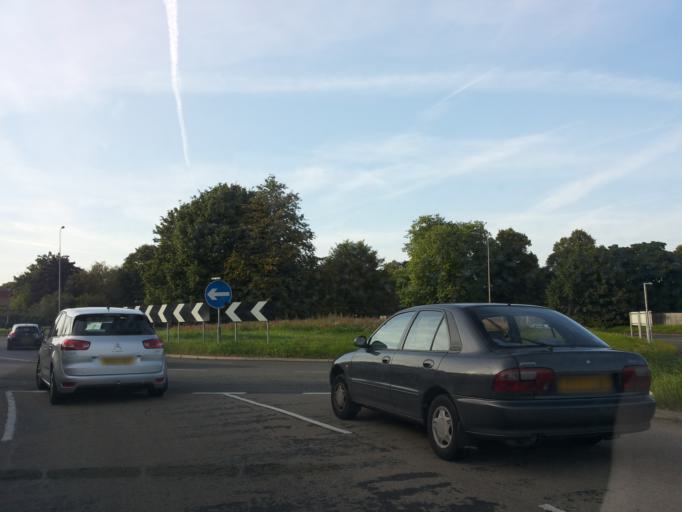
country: GB
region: England
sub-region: Staffordshire
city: Stone
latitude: 52.8865
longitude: -2.1357
